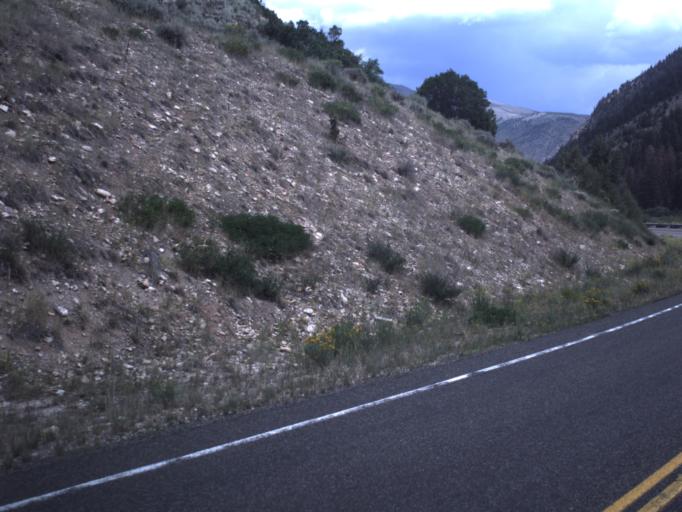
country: US
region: Utah
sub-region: Summit County
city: Francis
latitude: 40.4541
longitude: -110.8594
